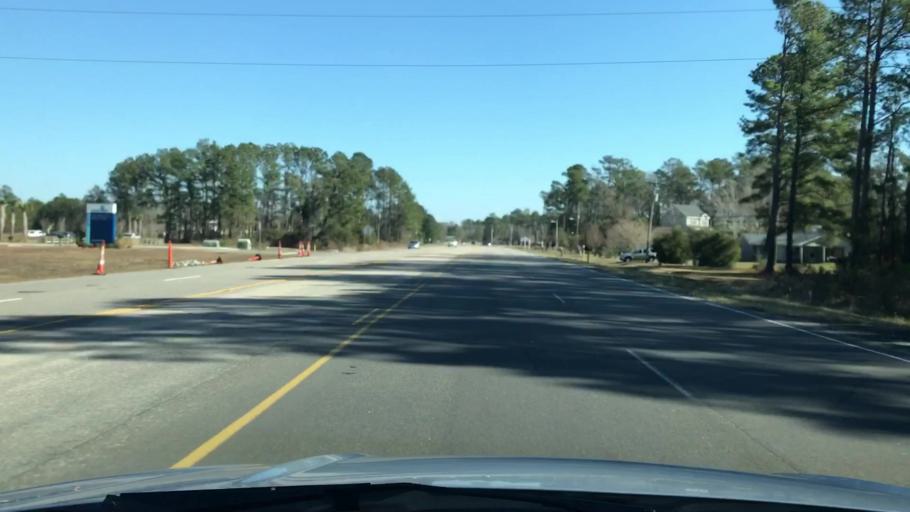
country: US
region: South Carolina
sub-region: Horry County
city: Garden City
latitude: 33.6299
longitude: -79.0280
